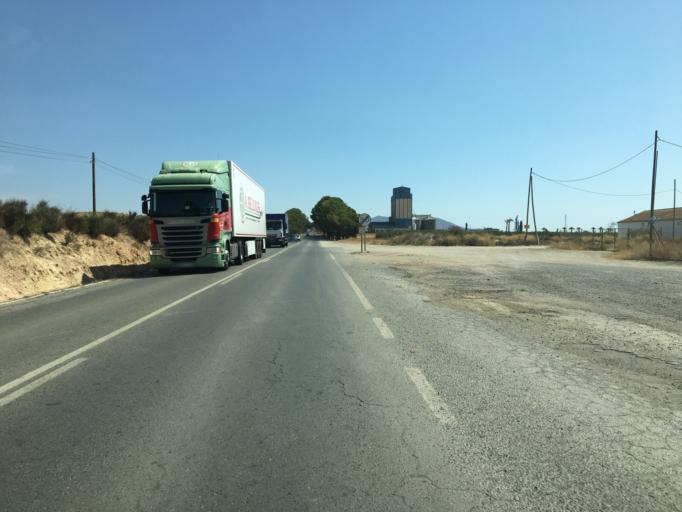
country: ES
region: Andalusia
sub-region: Provincia de Almeria
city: Huercal-Overa
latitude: 37.4114
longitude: -1.9298
